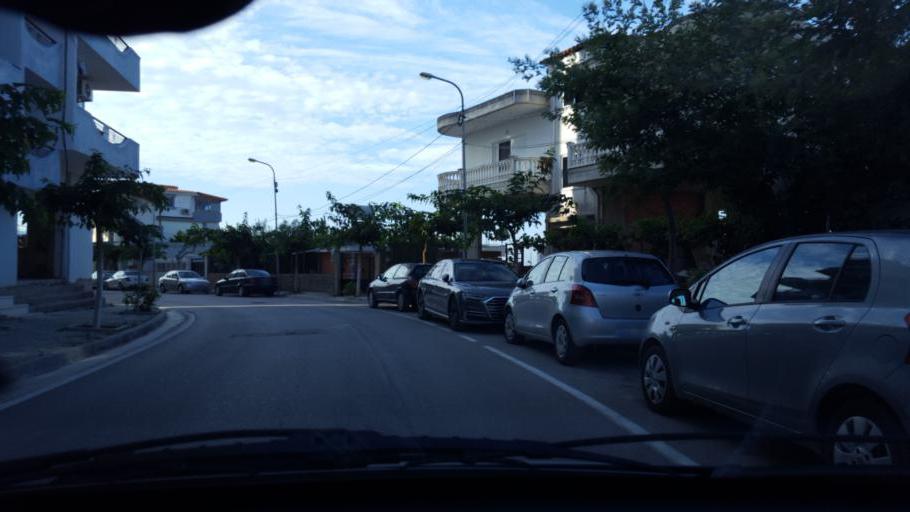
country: AL
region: Vlore
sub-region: Rrethi i Sarandes
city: Sarande
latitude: 39.8734
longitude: 19.9913
